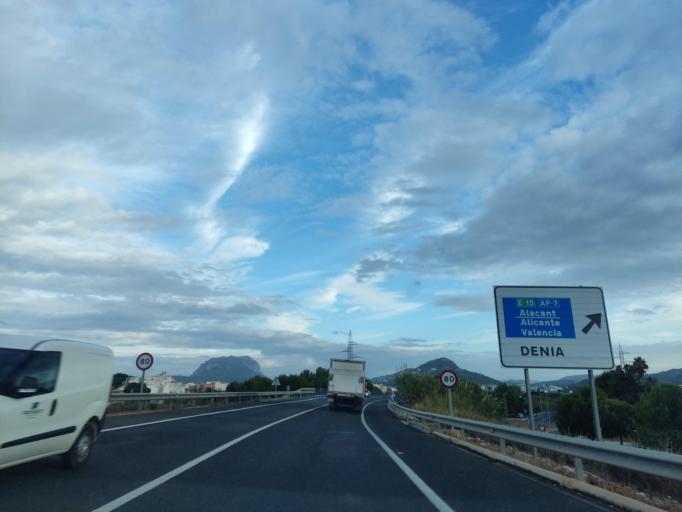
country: ES
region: Valencia
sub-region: Provincia de Alicante
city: Ondara
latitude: 38.8254
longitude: 0.0114
